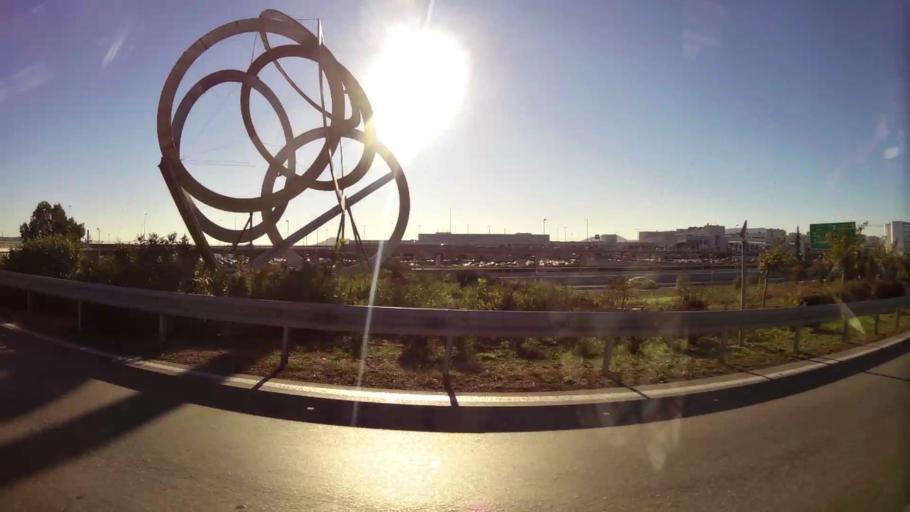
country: GR
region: Attica
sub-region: Nomarchia Anatolikis Attikis
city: Spata
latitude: 37.9402
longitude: 23.9466
